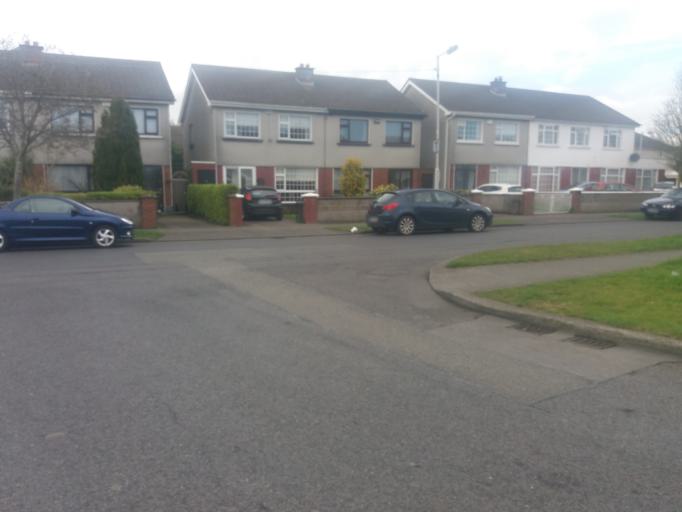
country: IE
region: Leinster
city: Ballymun
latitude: 53.3936
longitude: -6.2790
